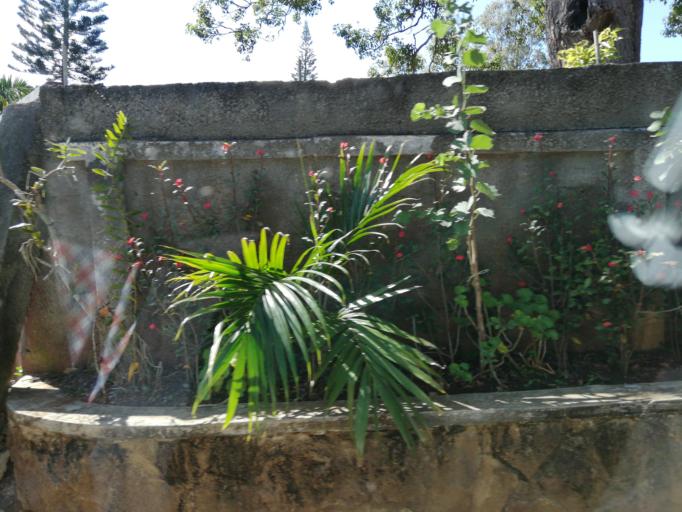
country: MU
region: Moka
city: Moka
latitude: -20.2172
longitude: 57.4917
